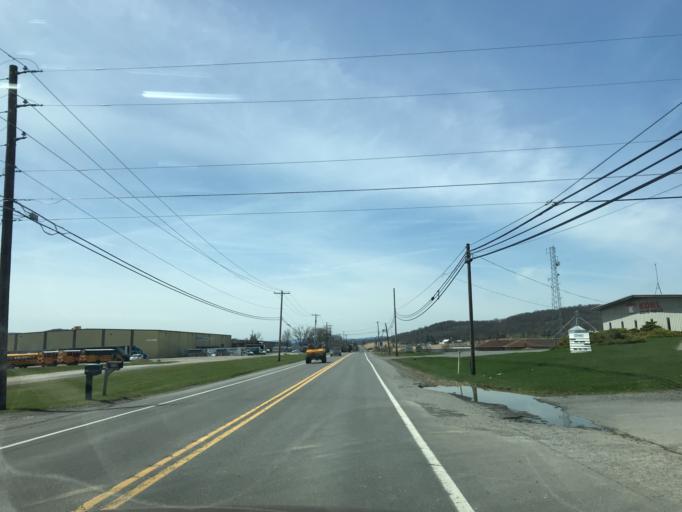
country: US
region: Pennsylvania
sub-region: Snyder County
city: Selinsgrove
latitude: 40.8057
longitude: -76.9103
